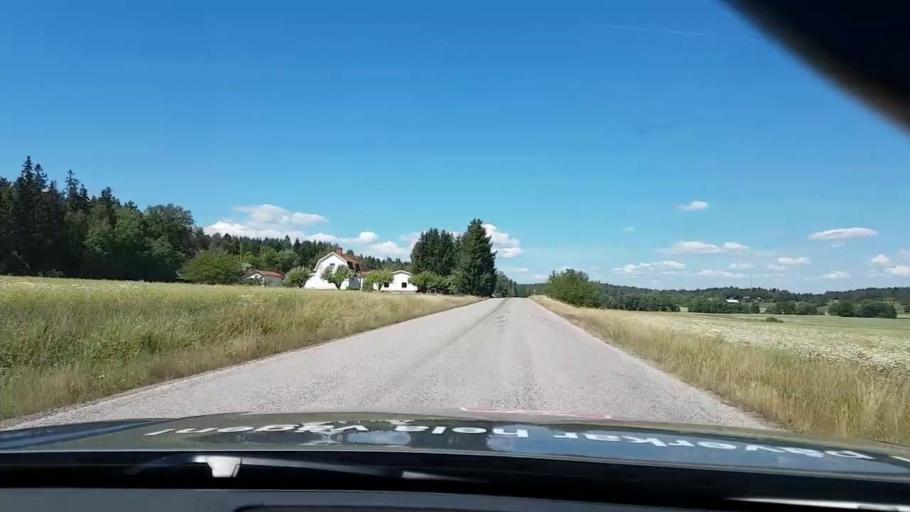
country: SE
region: Kalmar
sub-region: Vasterviks Kommun
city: Forserum
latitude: 57.9420
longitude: 16.4523
